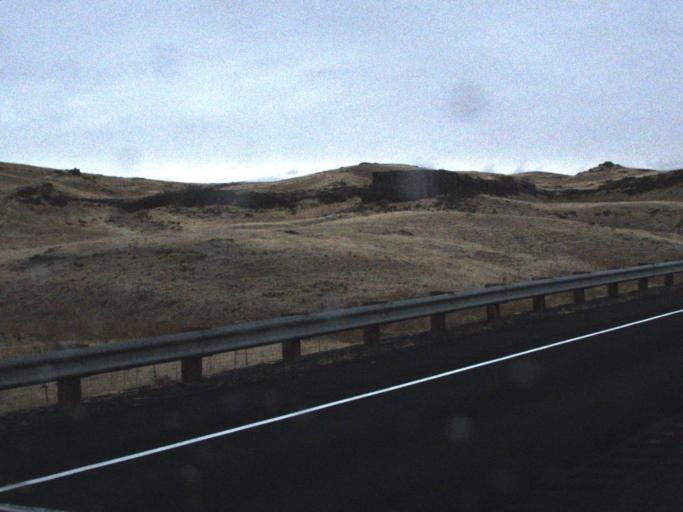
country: US
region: Washington
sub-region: Adams County
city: Ritzville
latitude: 46.7705
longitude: -118.1192
